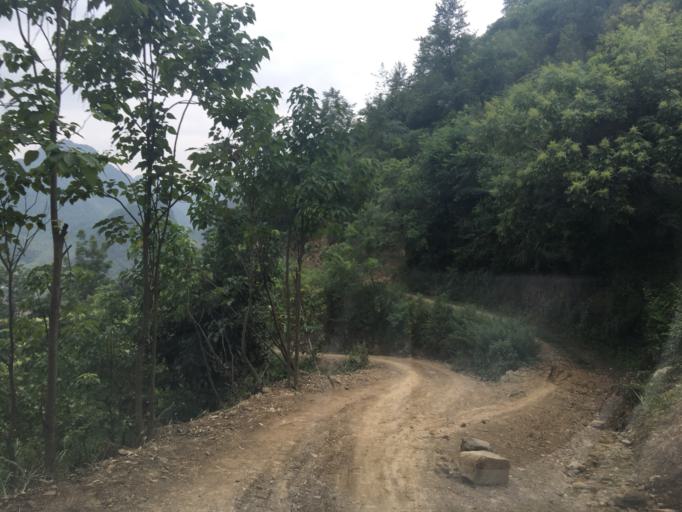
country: CN
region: Guangxi Zhuangzu Zizhiqu
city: Xinzhou
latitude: 25.1632
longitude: 105.6831
